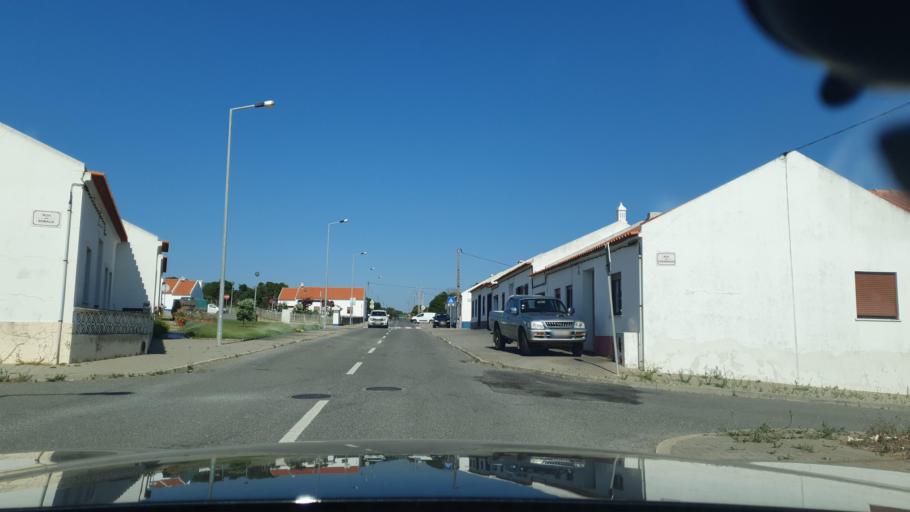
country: PT
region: Beja
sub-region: Odemira
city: Sao Teotonio
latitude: 37.4647
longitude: -8.7954
